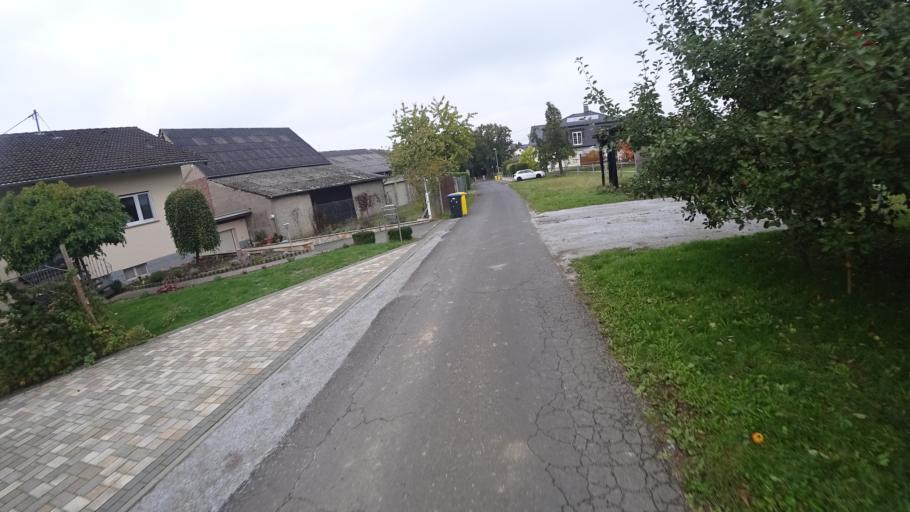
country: DE
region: Rheinland-Pfalz
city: Eppenrod
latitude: 50.4043
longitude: 7.9313
